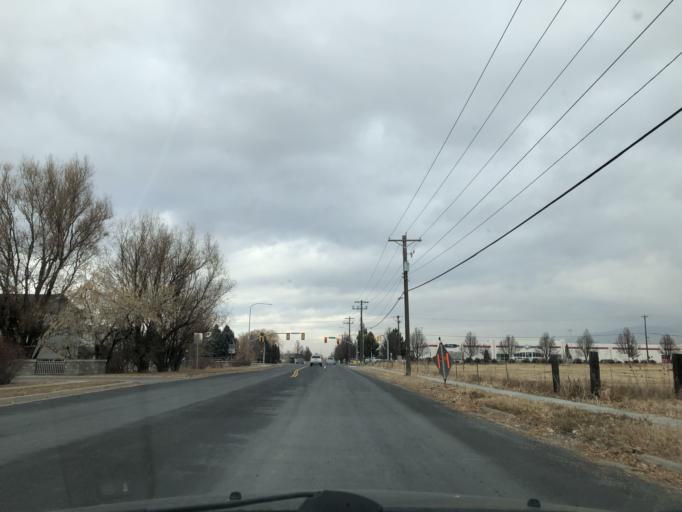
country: US
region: Utah
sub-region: Cache County
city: Logan
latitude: 41.7566
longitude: -111.8392
